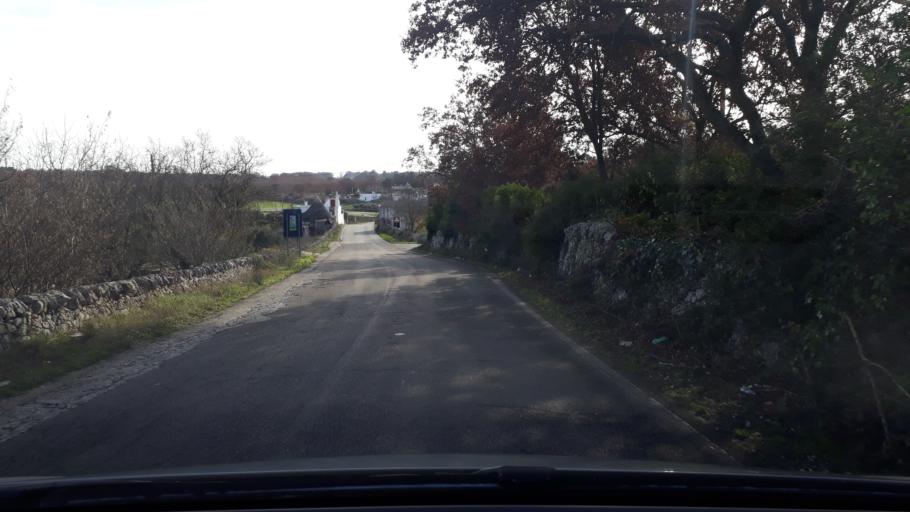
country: IT
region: Apulia
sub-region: Provincia di Taranto
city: Martina Franca
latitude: 40.6816
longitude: 17.3543
